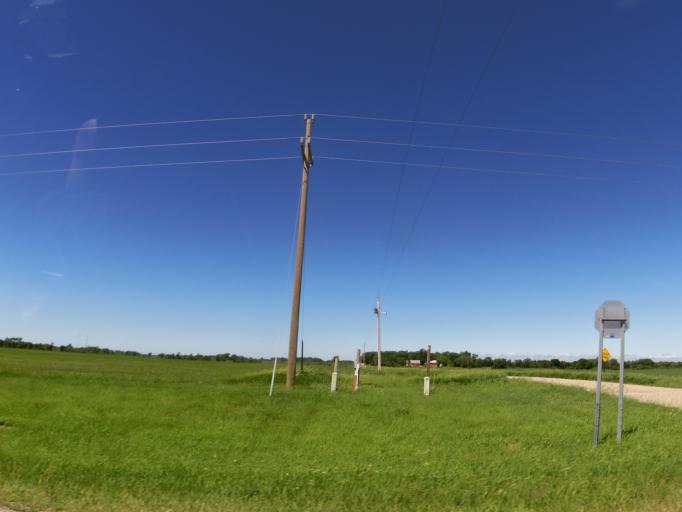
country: US
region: Minnesota
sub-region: Polk County
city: Fosston
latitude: 47.5715
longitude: -95.9821
